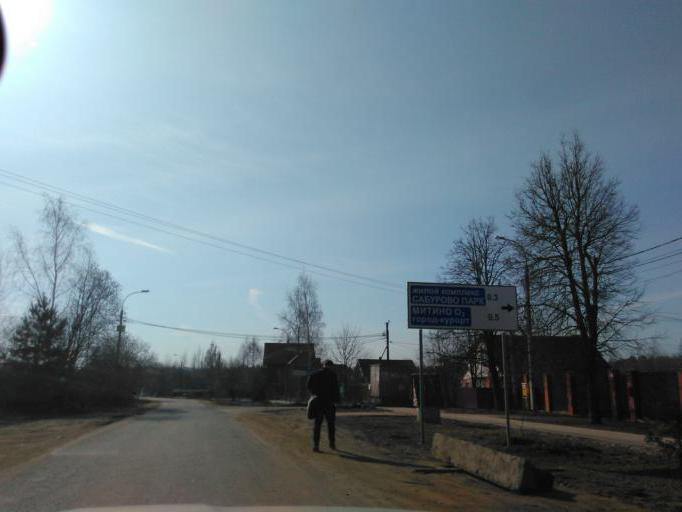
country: RU
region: Moskovskaya
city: Opalikha
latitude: 55.8789
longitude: 37.2658
